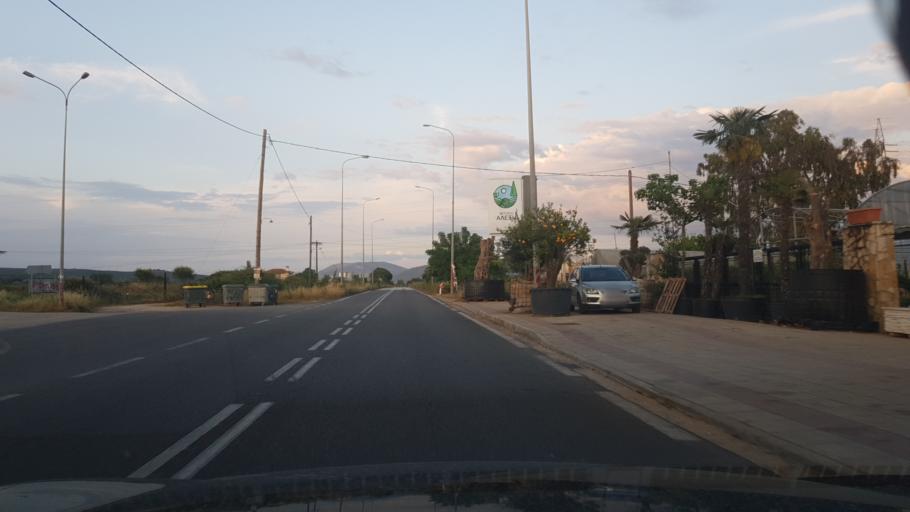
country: GR
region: West Greece
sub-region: Nomos Aitolias kai Akarnanias
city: Vonitsa
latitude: 38.8706
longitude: 20.8073
